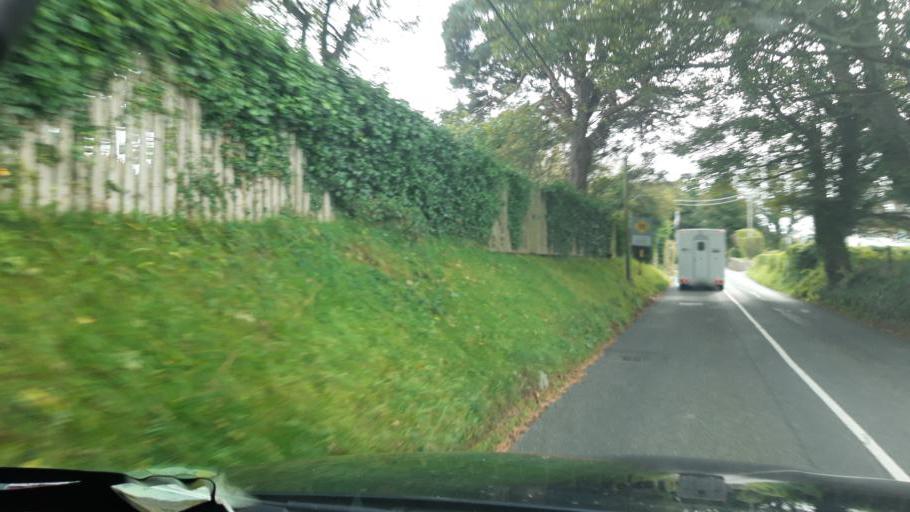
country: IE
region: Leinster
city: Foxrock
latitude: 53.2315
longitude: -6.1998
